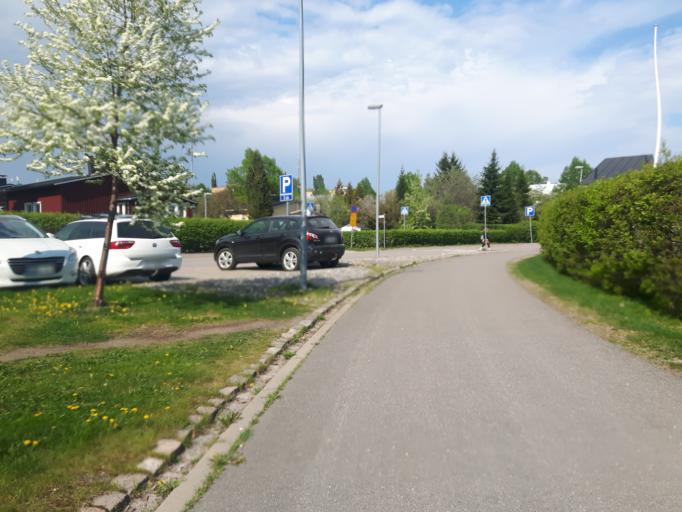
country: FI
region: Uusimaa
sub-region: Porvoo
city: Porvoo
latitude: 60.3943
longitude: 25.6716
